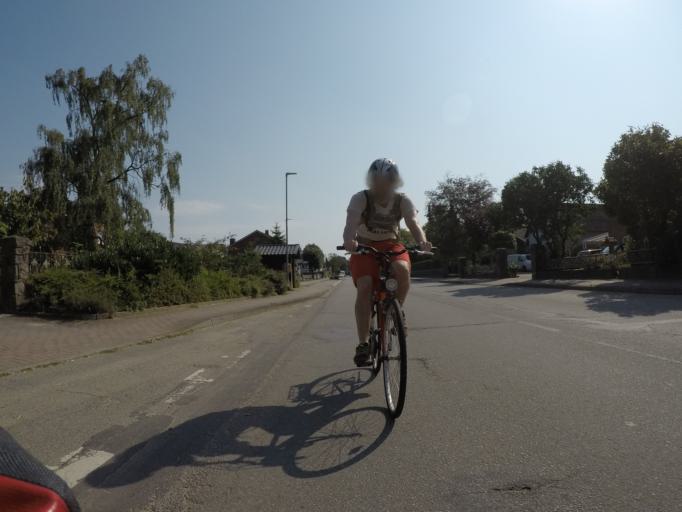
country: DE
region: Schleswig-Holstein
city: Todesfelde
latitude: 53.8939
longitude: 10.1761
